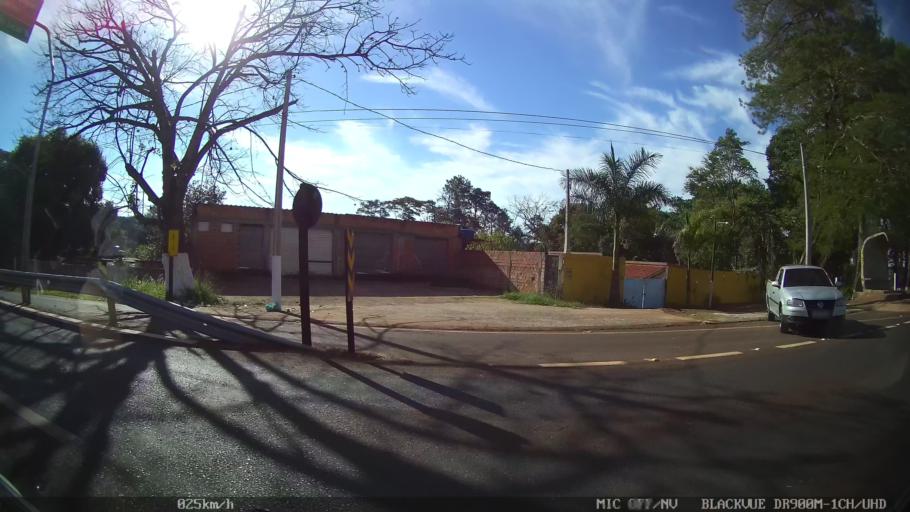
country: BR
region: Sao Paulo
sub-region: Araraquara
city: Araraquara
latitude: -21.7902
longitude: -48.1413
